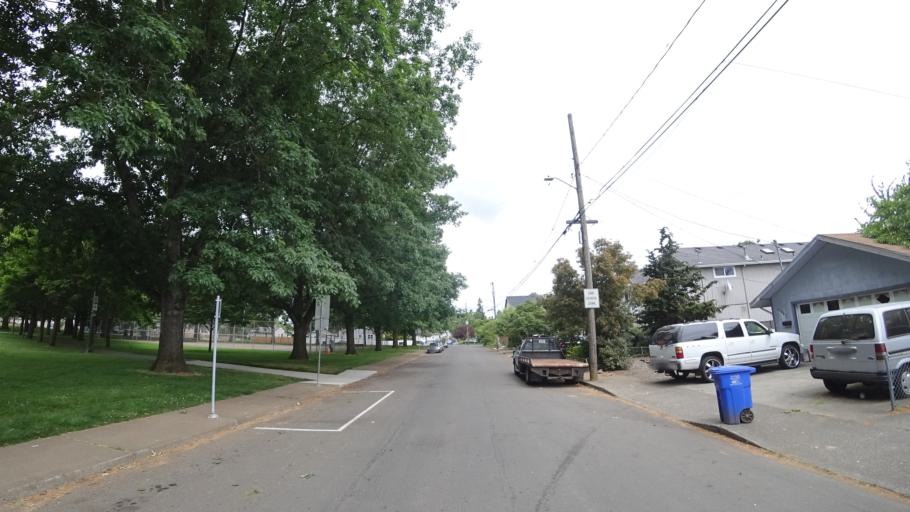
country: US
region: Oregon
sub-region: Multnomah County
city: Lents
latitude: 45.4739
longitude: -122.5717
